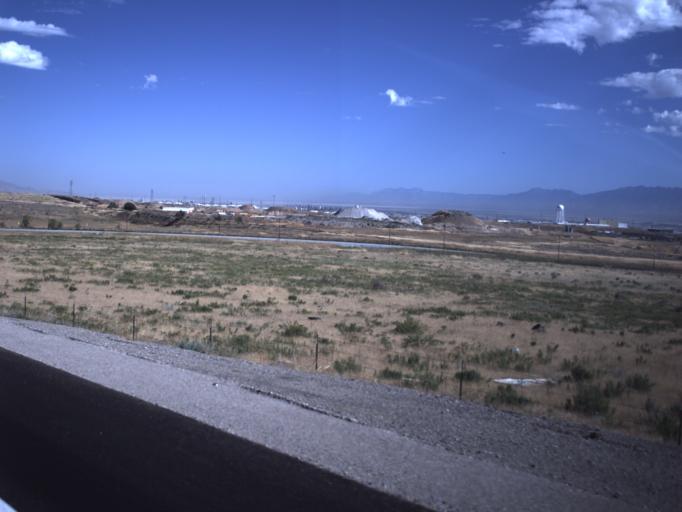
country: US
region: Utah
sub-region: Salt Lake County
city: Oquirrh
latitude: 40.6363
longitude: -112.0567
